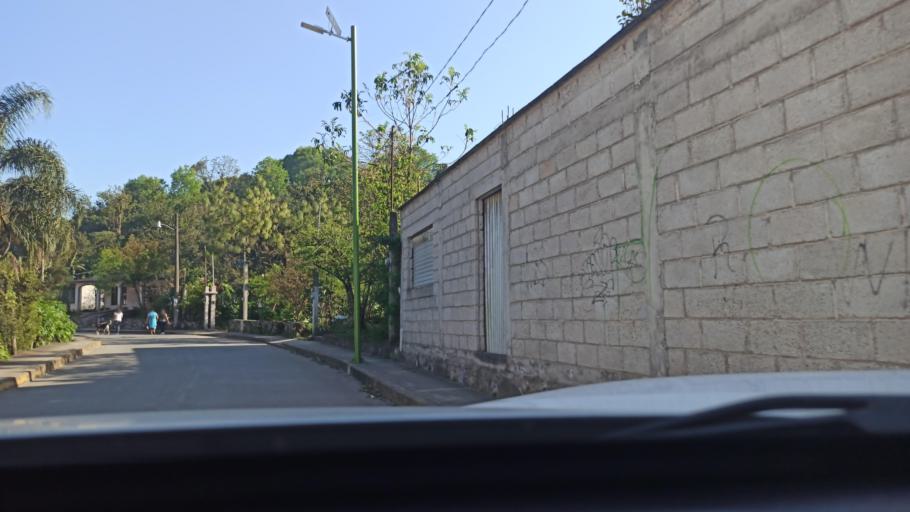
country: MX
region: Veracruz
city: Atzacan
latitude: 18.9066
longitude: -97.0872
